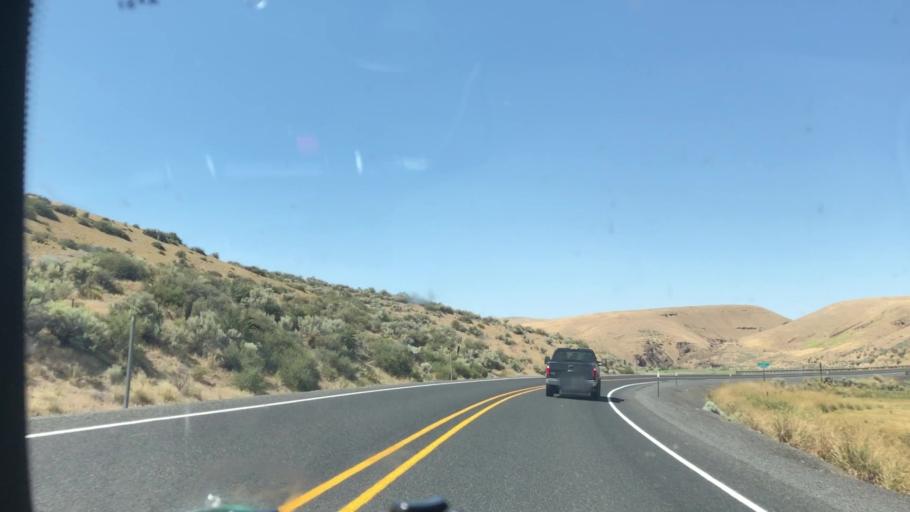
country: US
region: Idaho
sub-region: Owyhee County
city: Marsing
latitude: 43.2257
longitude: -117.0536
